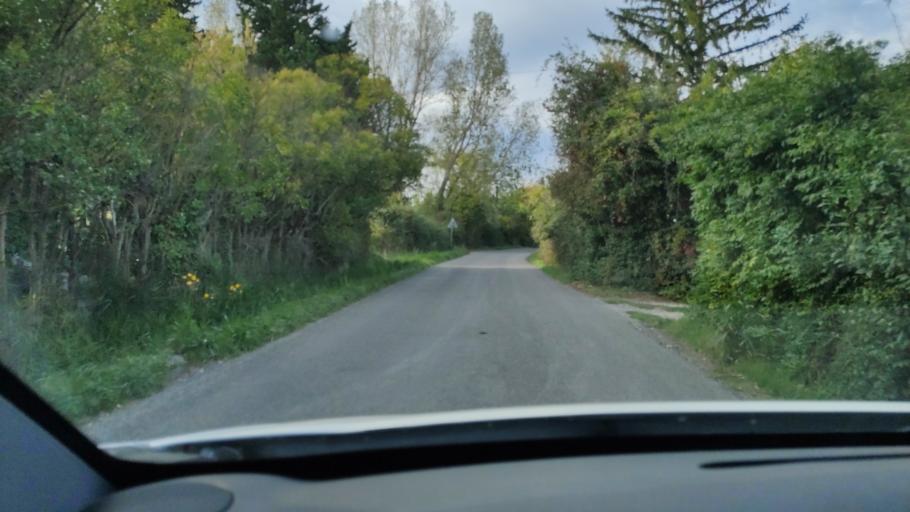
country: FR
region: Provence-Alpes-Cote d'Azur
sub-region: Departement du Vaucluse
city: Montfavet
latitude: 43.9199
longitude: 4.8454
